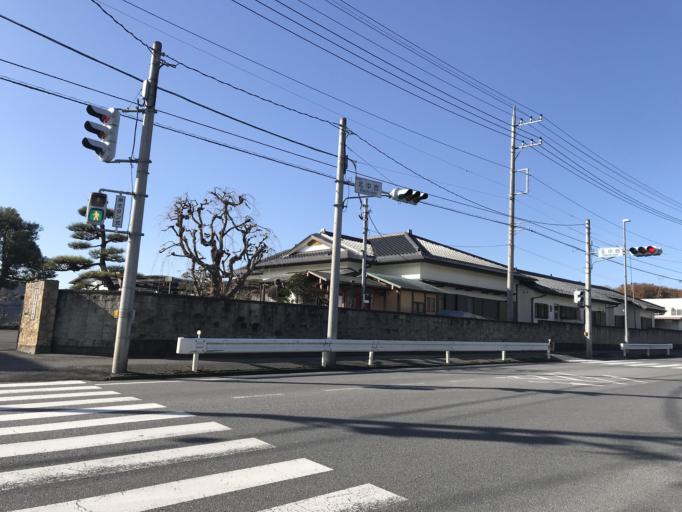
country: JP
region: Tochigi
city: Kanuma
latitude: 36.5823
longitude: 139.7513
